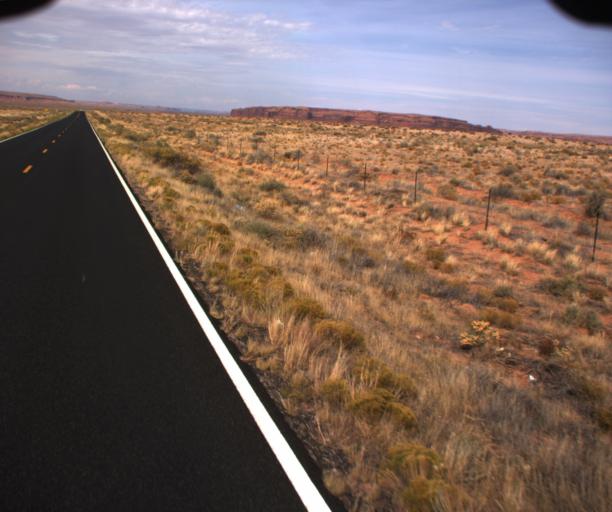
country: US
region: Arizona
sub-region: Apache County
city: Many Farms
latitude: 36.5562
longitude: -109.5358
